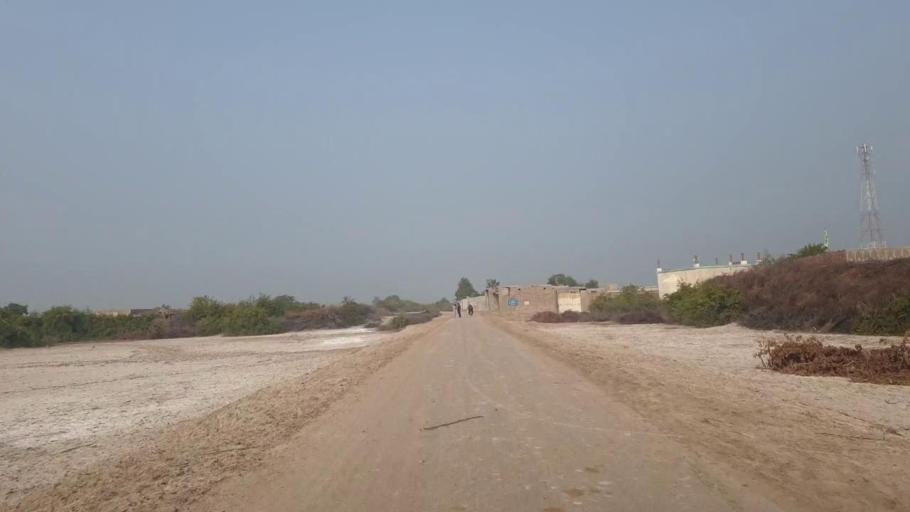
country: PK
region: Sindh
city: Bhit Shah
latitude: 25.8527
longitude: 68.5646
